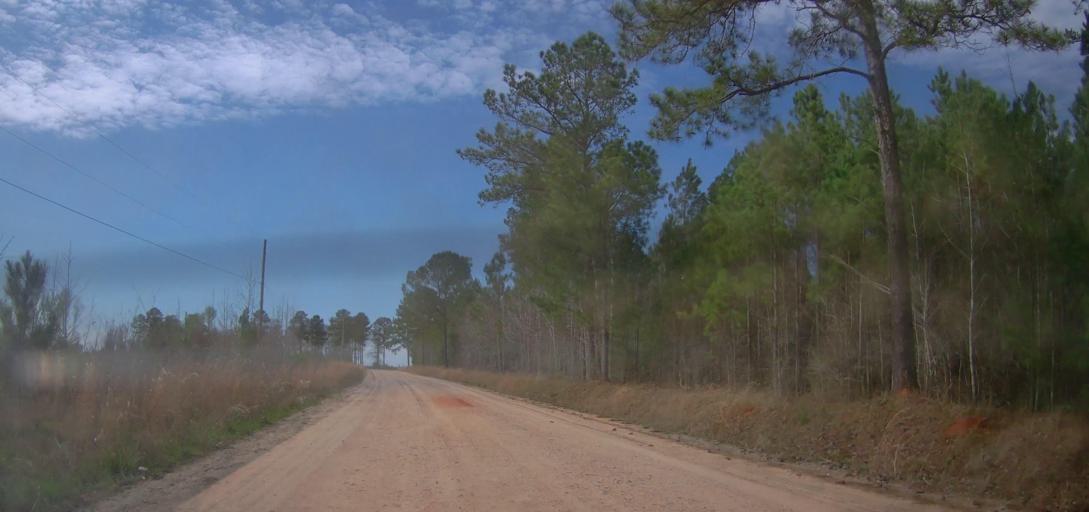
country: US
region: Georgia
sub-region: Monroe County
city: Forsyth
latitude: 33.0313
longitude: -83.8801
